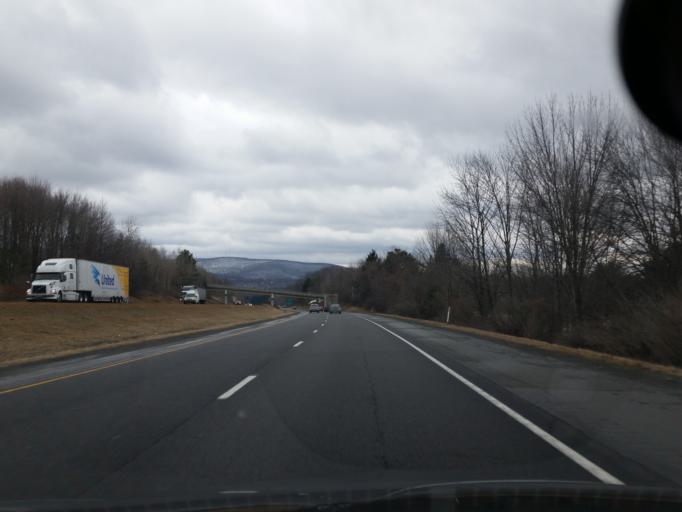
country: US
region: Pennsylvania
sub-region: Lackawanna County
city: Clarks Green
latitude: 41.5087
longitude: -75.6713
